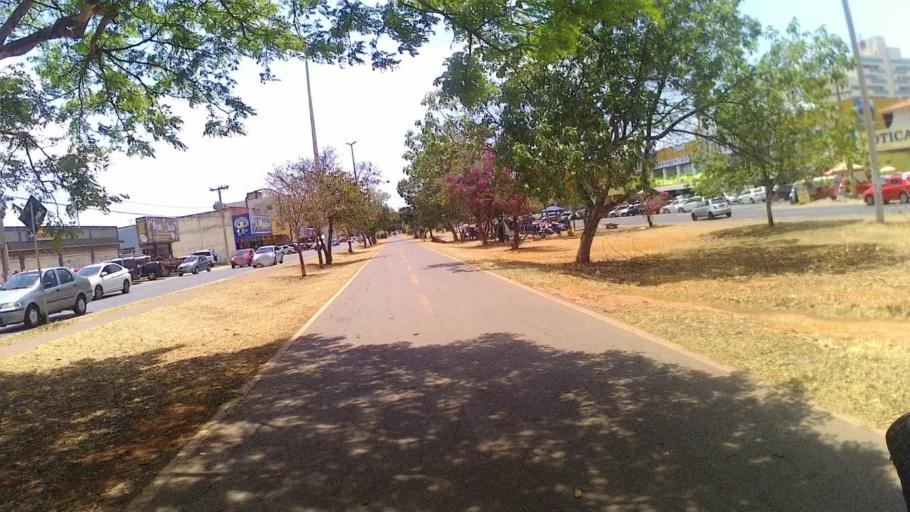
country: BR
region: Federal District
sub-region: Brasilia
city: Brasilia
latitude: -15.8734
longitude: -48.0720
